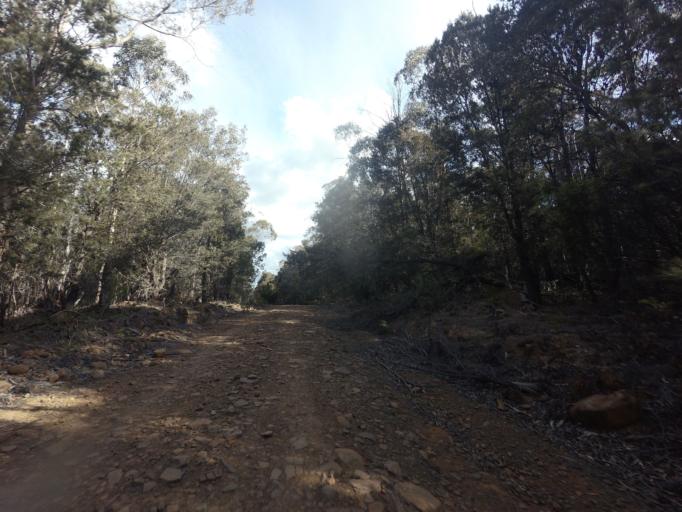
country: AU
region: Tasmania
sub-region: Break O'Day
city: St Helens
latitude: -41.8414
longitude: 148.0865
